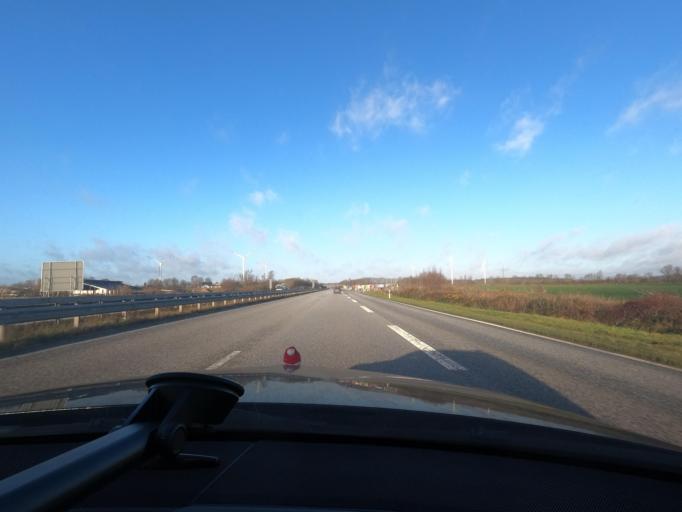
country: DE
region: Schleswig-Holstein
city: Bollingstedt
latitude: 54.6324
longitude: 9.4399
